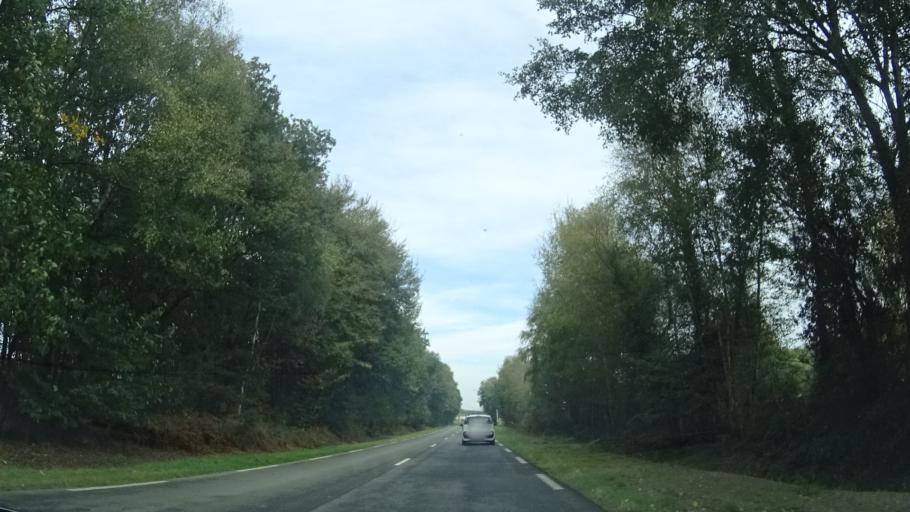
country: FR
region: Brittany
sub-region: Departement d'Ille-et-Vilaine
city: Quebriac
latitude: 48.3453
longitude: -1.7835
